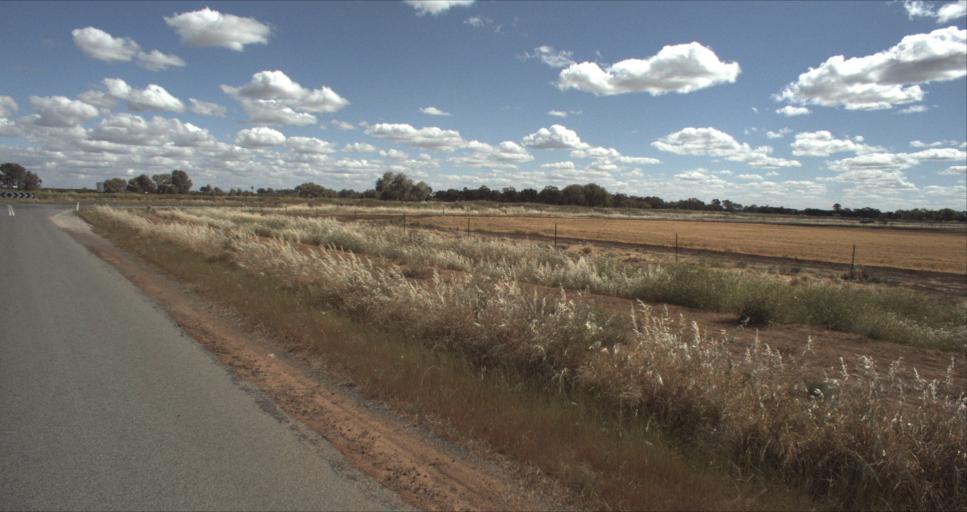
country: AU
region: New South Wales
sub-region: Leeton
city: Leeton
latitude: -34.5033
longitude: 146.2450
